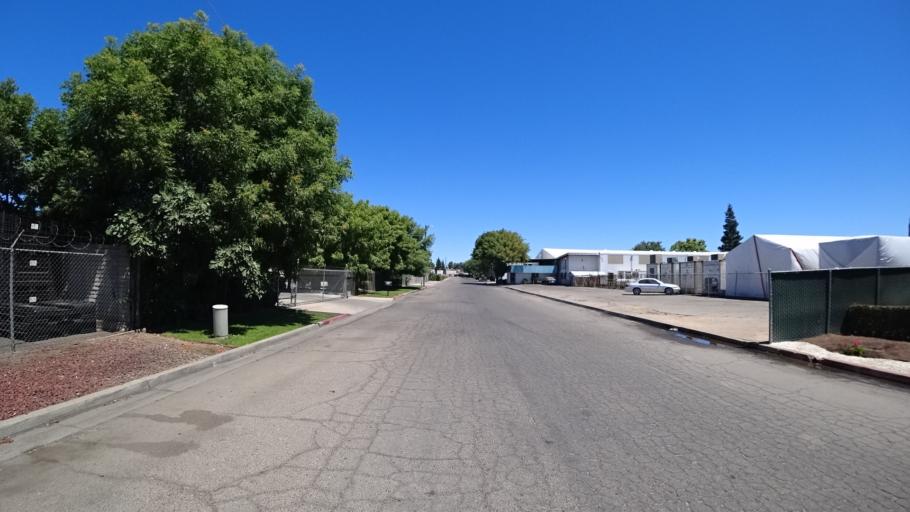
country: US
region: California
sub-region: Fresno County
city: West Park
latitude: 36.7887
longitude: -119.8500
